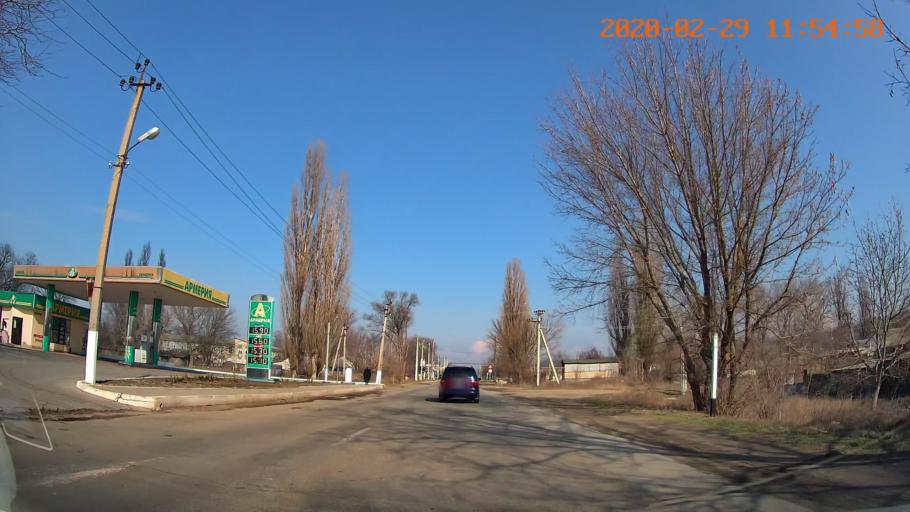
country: MD
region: Telenesti
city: Ribnita
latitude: 47.7873
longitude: 28.9967
